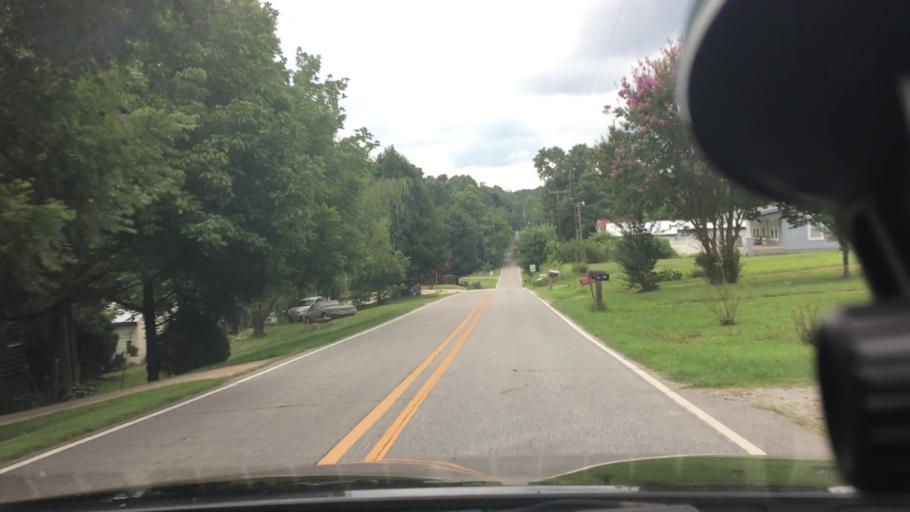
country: US
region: North Carolina
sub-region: McDowell County
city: West Marion
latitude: 35.6625
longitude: -82.0172
